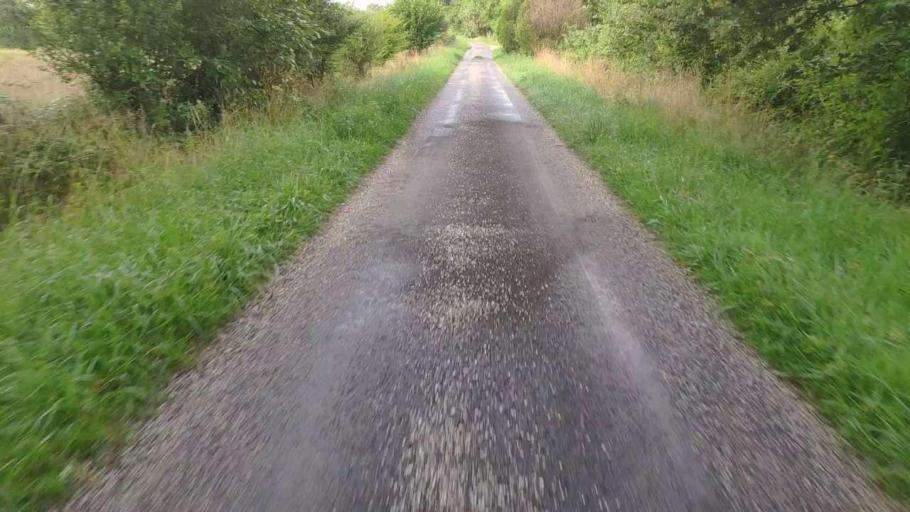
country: FR
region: Franche-Comte
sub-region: Departement du Jura
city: Mont-sous-Vaudrey
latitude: 46.8769
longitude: 5.5295
